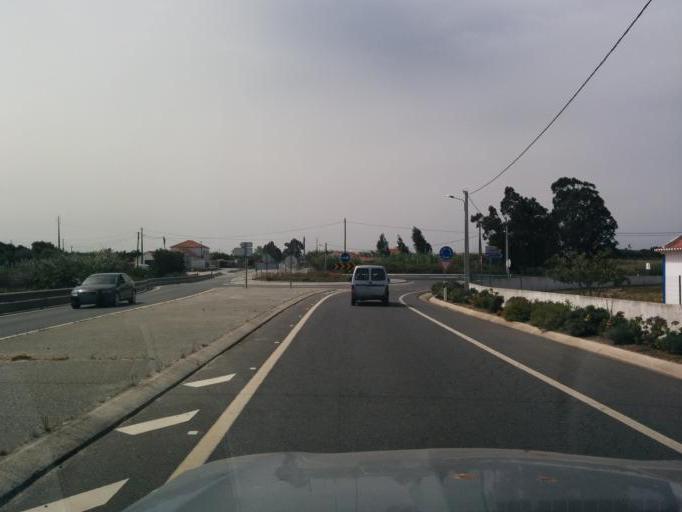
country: PT
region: Beja
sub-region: Odemira
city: Vila Nova de Milfontes
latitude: 37.6561
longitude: -8.7596
